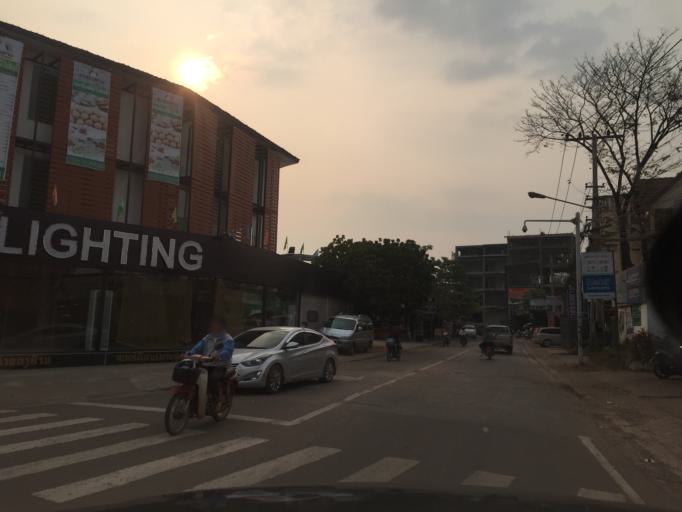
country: LA
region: Vientiane
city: Vientiane
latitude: 17.9754
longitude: 102.6096
